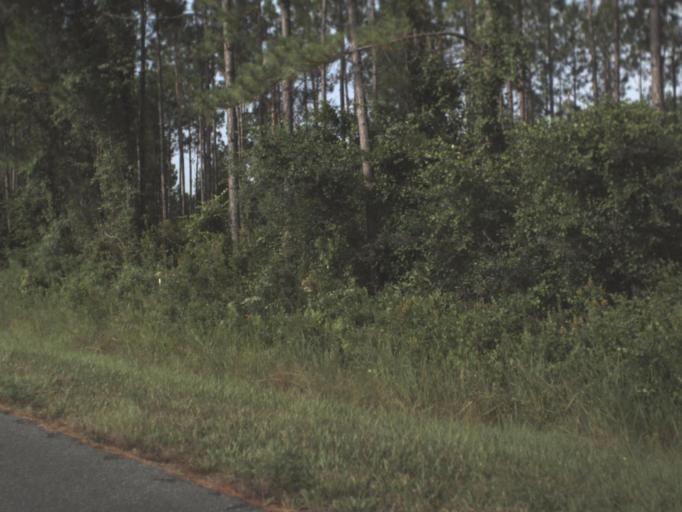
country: US
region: Florida
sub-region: Taylor County
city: Perry
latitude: 30.2290
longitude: -83.6168
